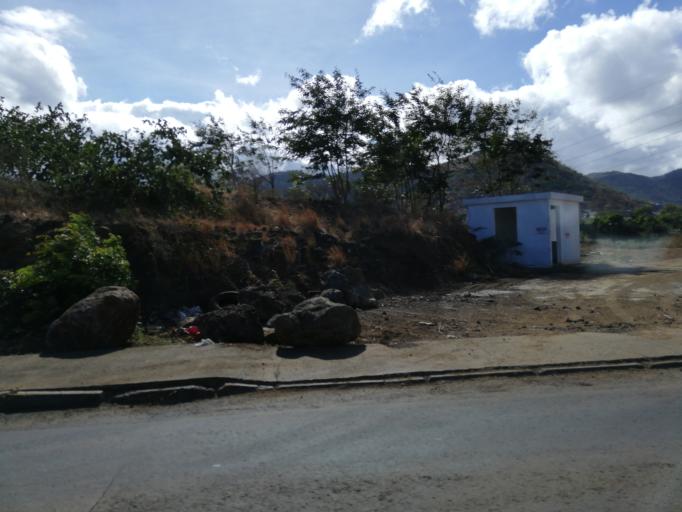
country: MU
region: Moka
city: Pailles
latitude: -20.1811
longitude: 57.4746
